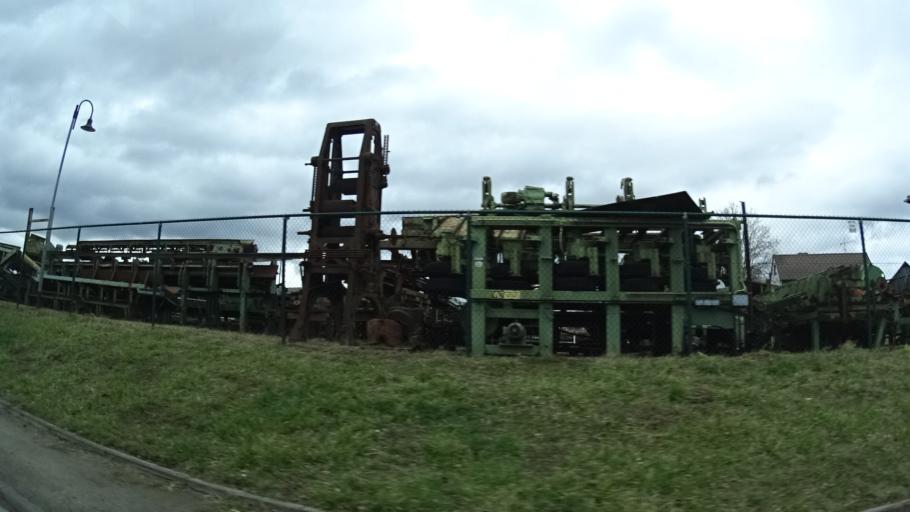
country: DE
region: Hesse
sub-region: Regierungsbezirk Giessen
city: Schlitz
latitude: 50.6697
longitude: 9.5549
